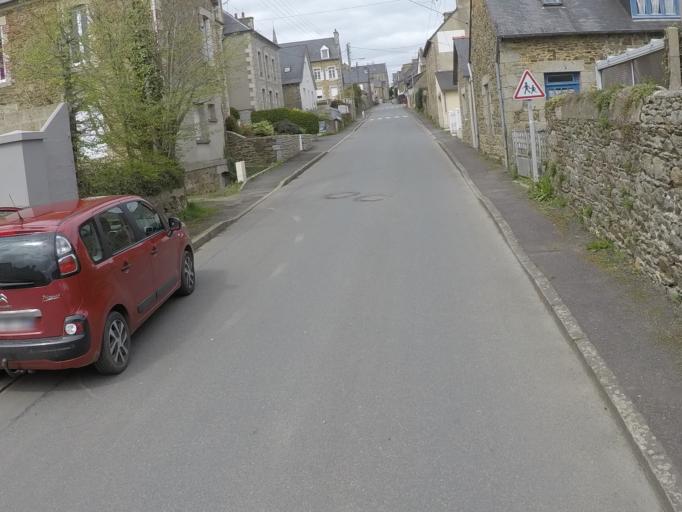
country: FR
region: Brittany
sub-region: Departement des Cotes-d'Armor
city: Plouha
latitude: 48.6734
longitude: -2.9265
